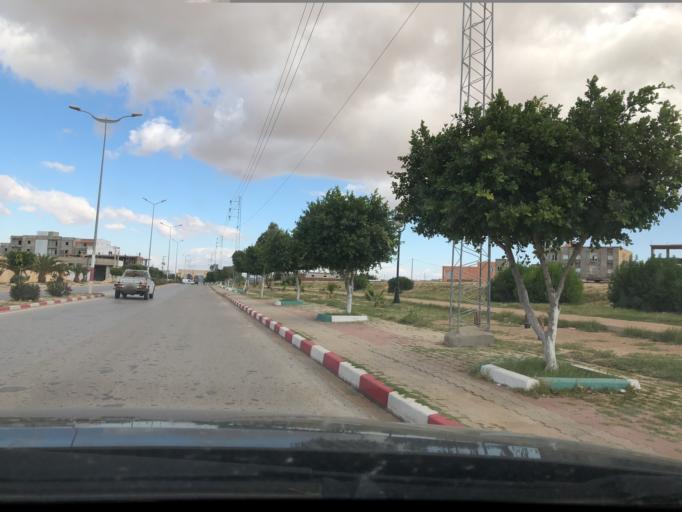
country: TN
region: Al Qasrayn
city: Kasserine
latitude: 35.1797
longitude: 8.8553
